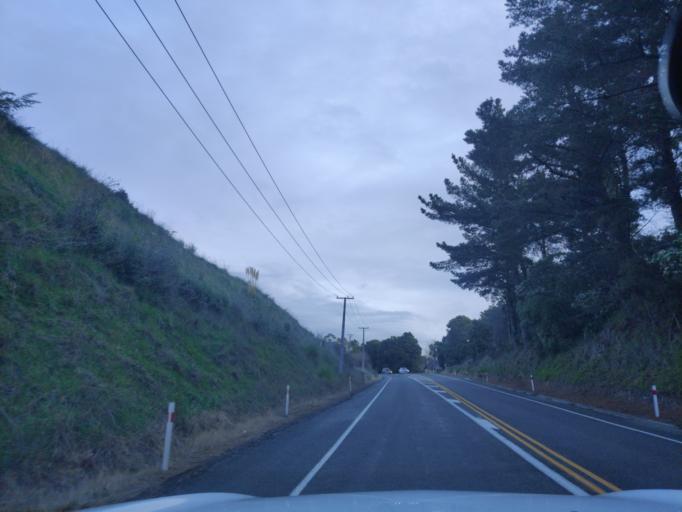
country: NZ
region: Manawatu-Wanganui
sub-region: Palmerston North City
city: Palmerston North
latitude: -40.3803
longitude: 175.6477
